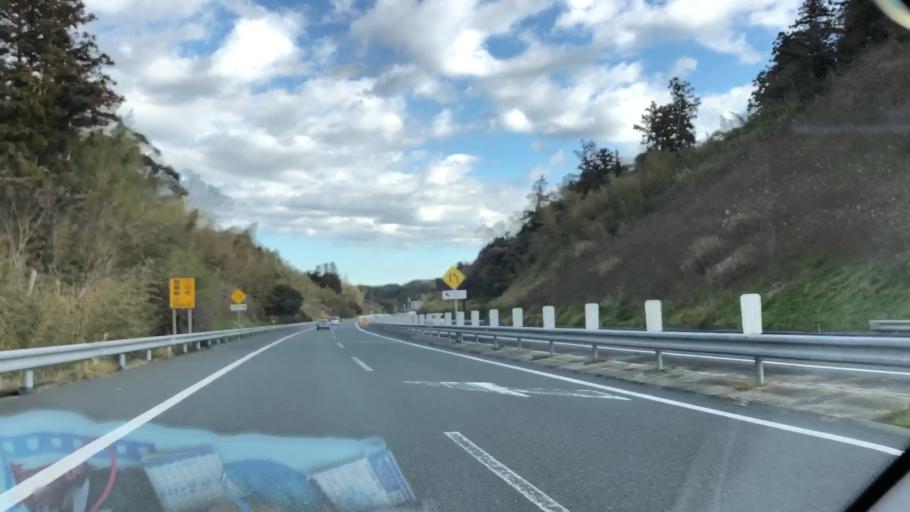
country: JP
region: Chiba
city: Kimitsu
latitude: 35.2565
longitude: 139.8939
